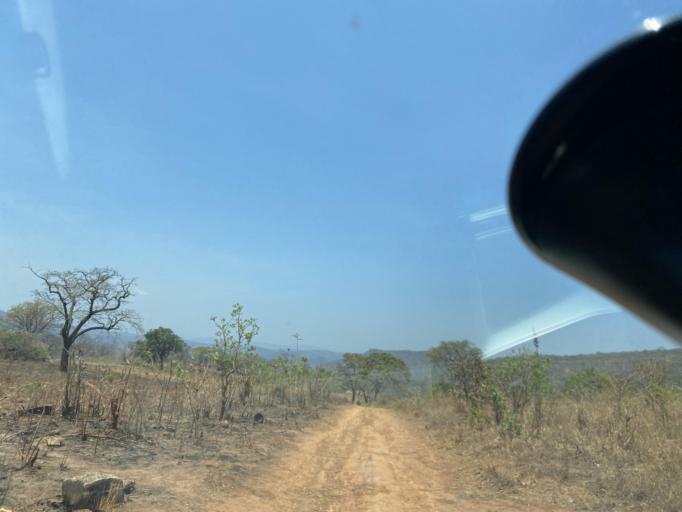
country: ZM
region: Lusaka
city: Kafue
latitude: -15.8051
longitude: 28.4426
